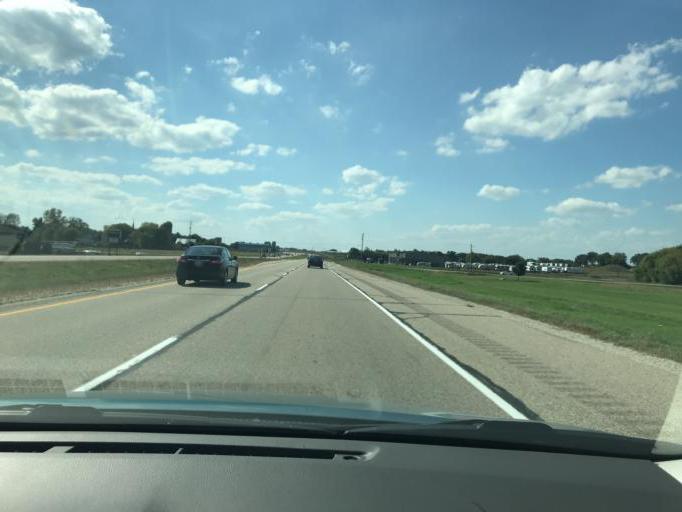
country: US
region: Wisconsin
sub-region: Kenosha County
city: Powers Lake
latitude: 42.5837
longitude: -88.2835
